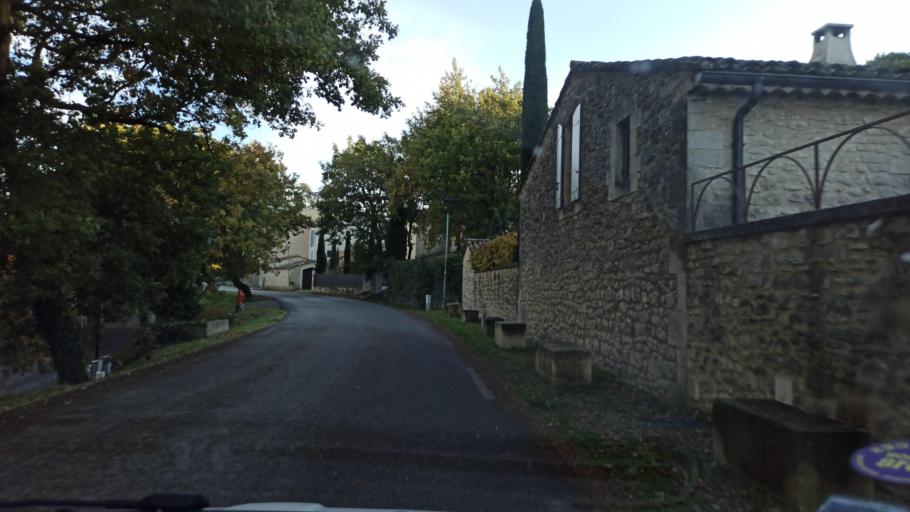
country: FR
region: Provence-Alpes-Cote d'Azur
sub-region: Departement du Vaucluse
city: Bonnieux
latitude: 43.8348
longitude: 5.2717
